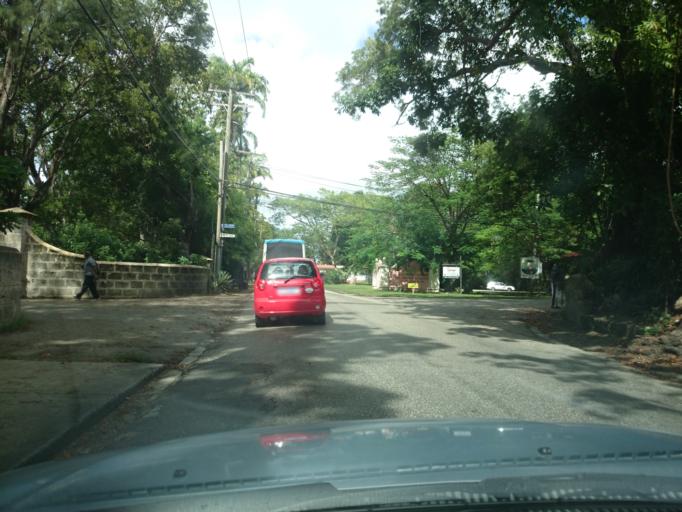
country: BB
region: Saint James
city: Holetown
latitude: 13.1948
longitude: -59.6387
